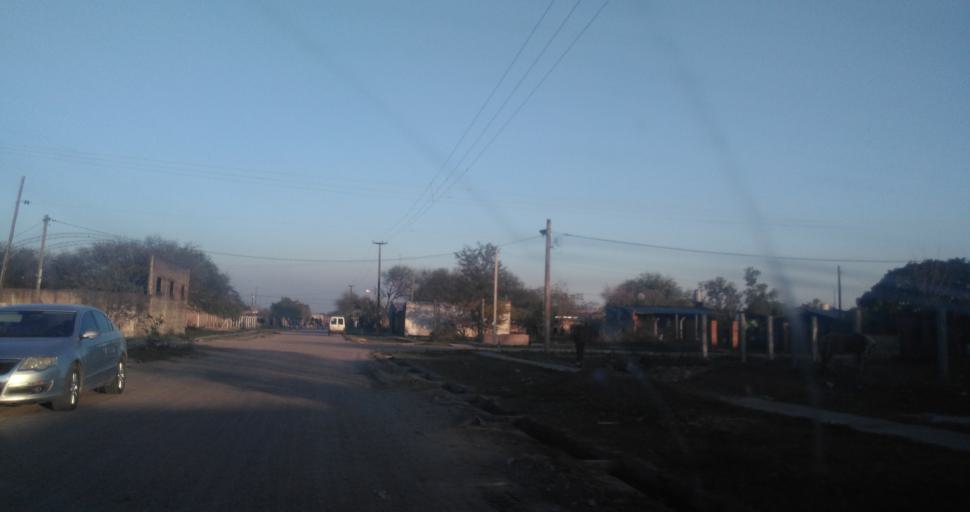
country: AR
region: Chaco
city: Resistencia
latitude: -27.4739
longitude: -59.0091
